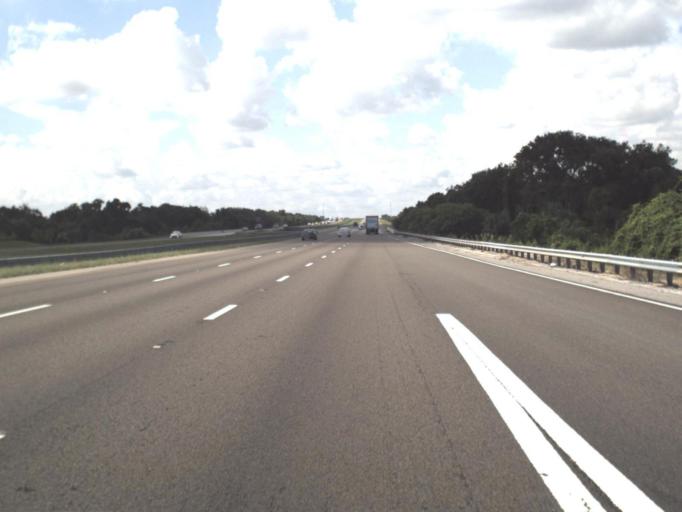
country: US
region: Florida
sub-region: Hillsborough County
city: Riverview
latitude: 27.8469
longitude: -82.3473
